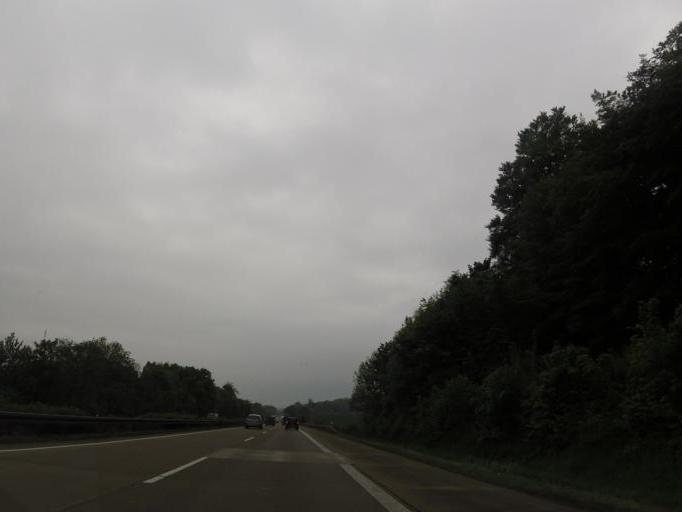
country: DE
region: Lower Saxony
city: Seesen
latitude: 51.8725
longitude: 10.1268
